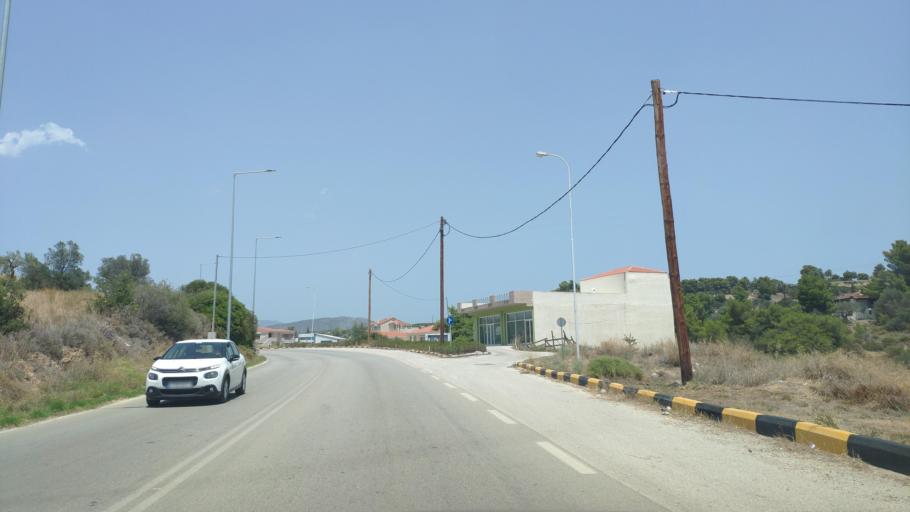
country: GR
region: Peloponnese
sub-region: Nomos Argolidos
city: Kranidi
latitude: 37.3564
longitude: 23.1600
